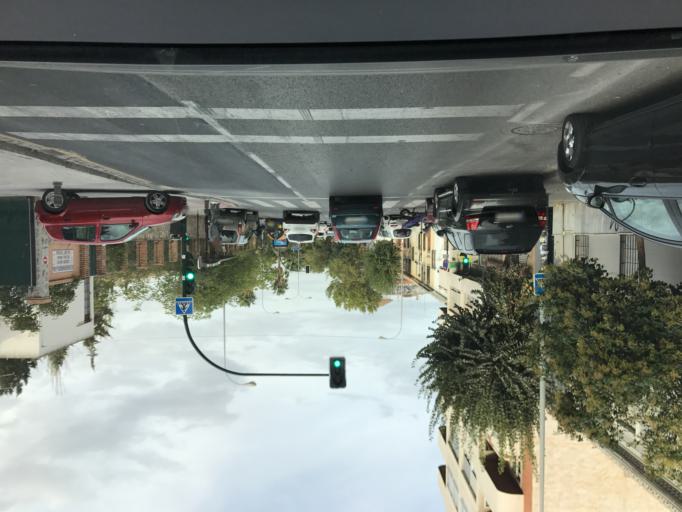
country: ES
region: Andalusia
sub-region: Provincia de Granada
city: Granada
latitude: 37.1887
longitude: -3.6004
